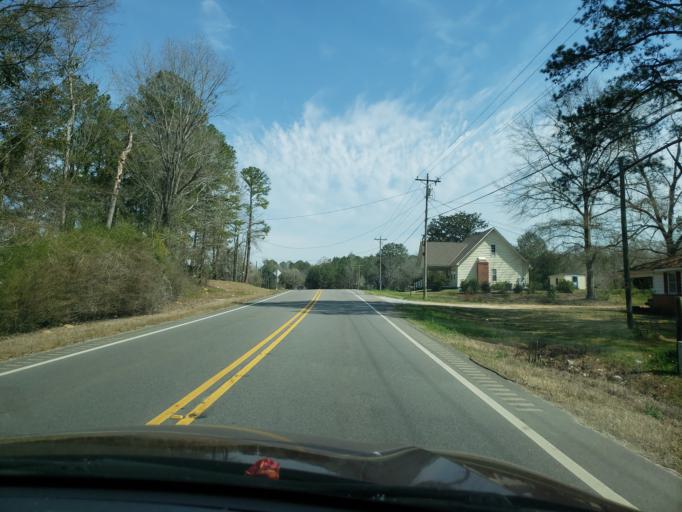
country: US
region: Alabama
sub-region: Elmore County
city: Wetumpka
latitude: 32.5571
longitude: -86.1492
